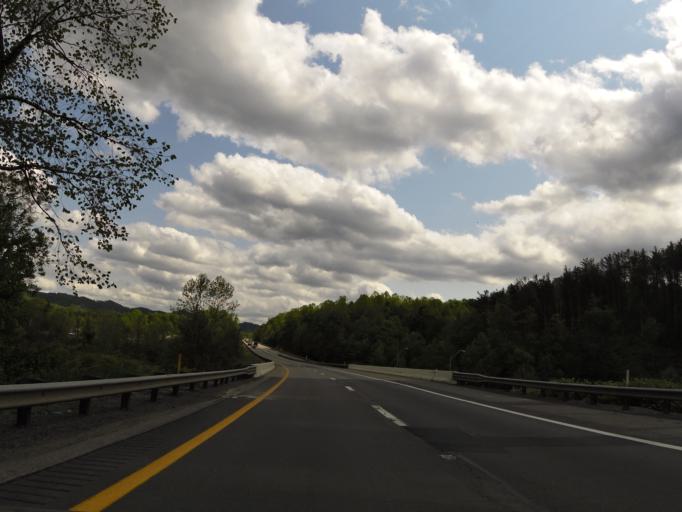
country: US
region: West Virginia
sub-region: Raleigh County
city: Bradley
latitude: 37.9169
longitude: -81.2709
